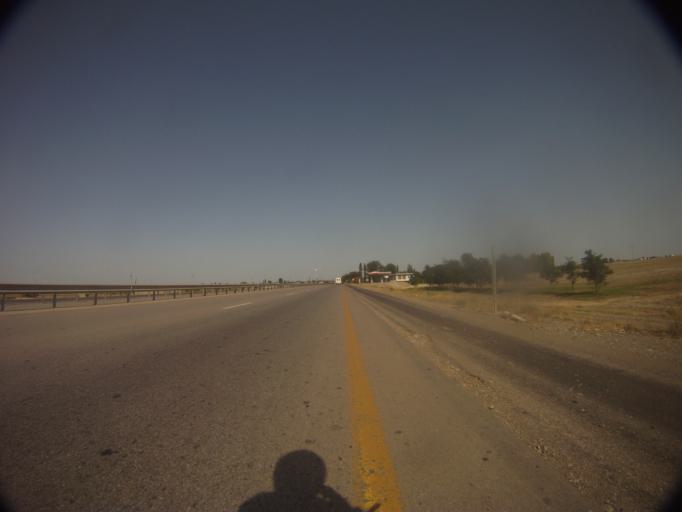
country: AZ
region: Samux
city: Samux
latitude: 40.6891
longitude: 46.5467
